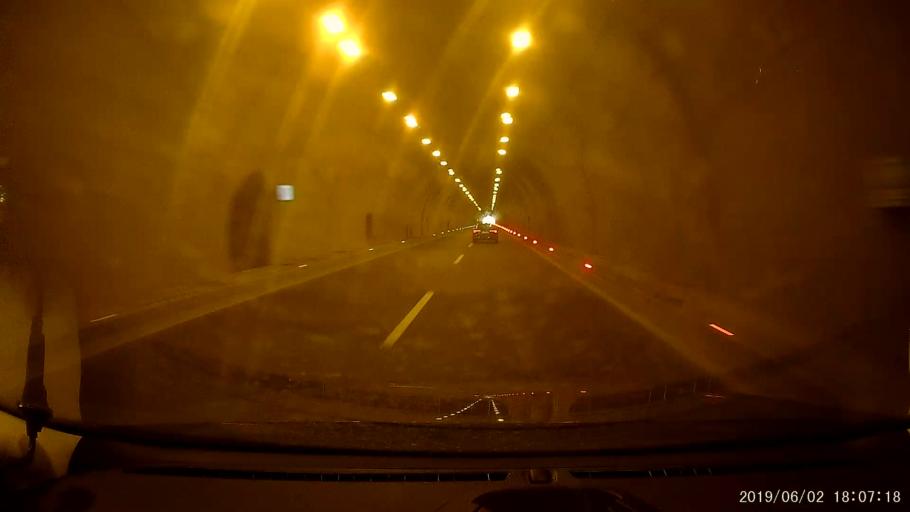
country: TR
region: Ordu
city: Unieh
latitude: 41.1142
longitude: 37.2811
